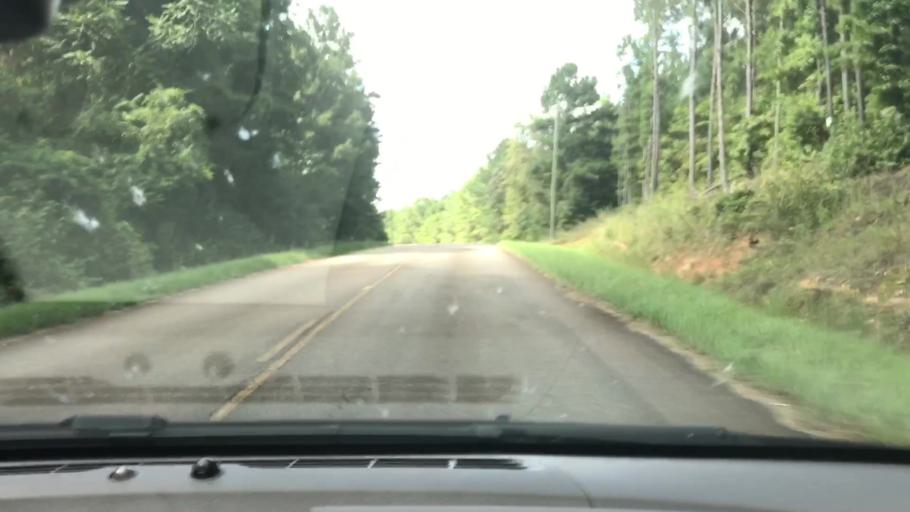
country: US
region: Georgia
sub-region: Troup County
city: La Grange
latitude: 33.1211
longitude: -85.1262
